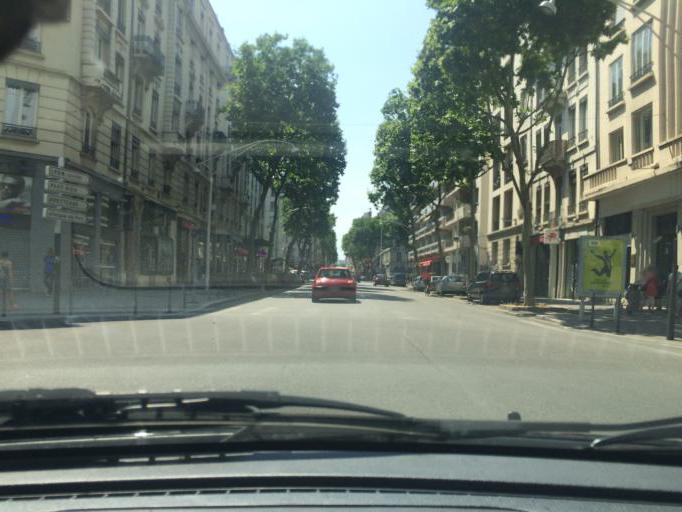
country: FR
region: Rhone-Alpes
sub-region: Departement du Rhone
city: Villeurbanne
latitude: 45.7701
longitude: 4.8592
